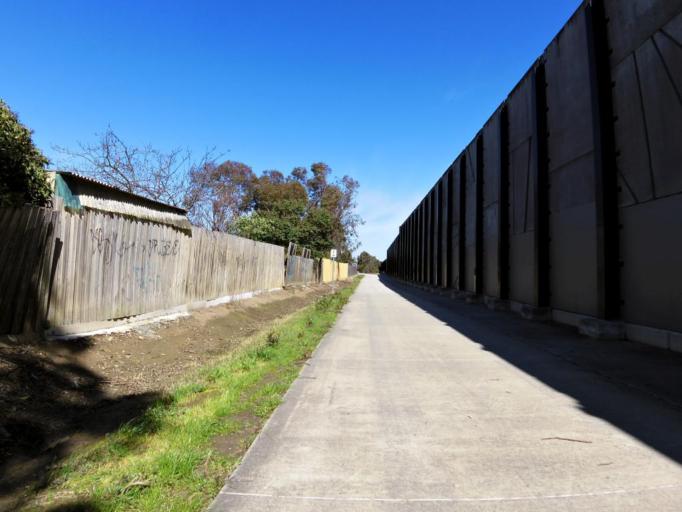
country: AU
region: Victoria
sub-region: Greater Dandenong
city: Dandenong North
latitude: -37.9597
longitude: 145.2007
